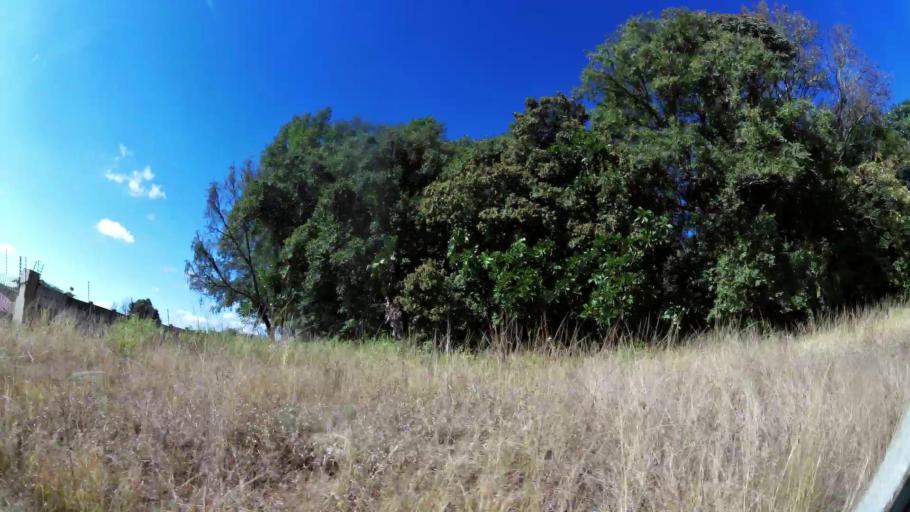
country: ZA
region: Limpopo
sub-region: Mopani District Municipality
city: Tzaneen
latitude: -23.8183
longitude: 30.1558
